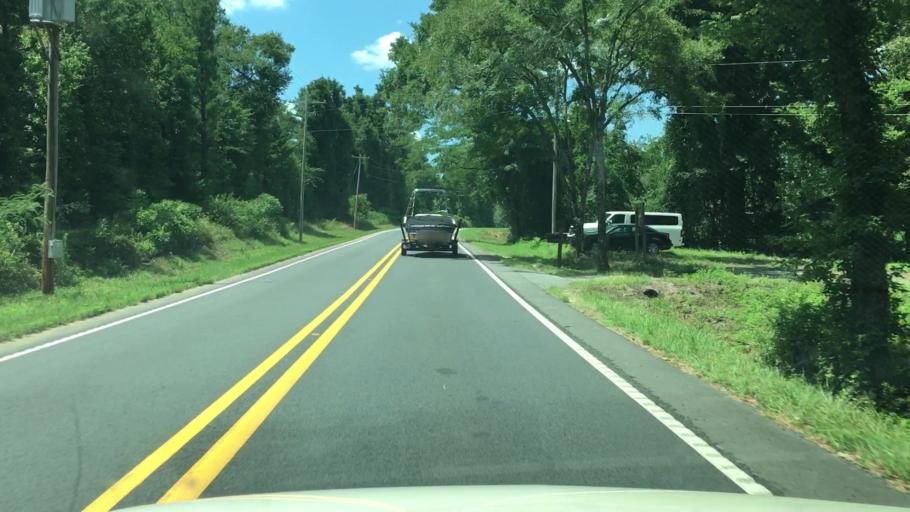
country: US
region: Arkansas
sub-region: Garland County
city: Lake Hamilton
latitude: 34.2721
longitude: -93.1478
